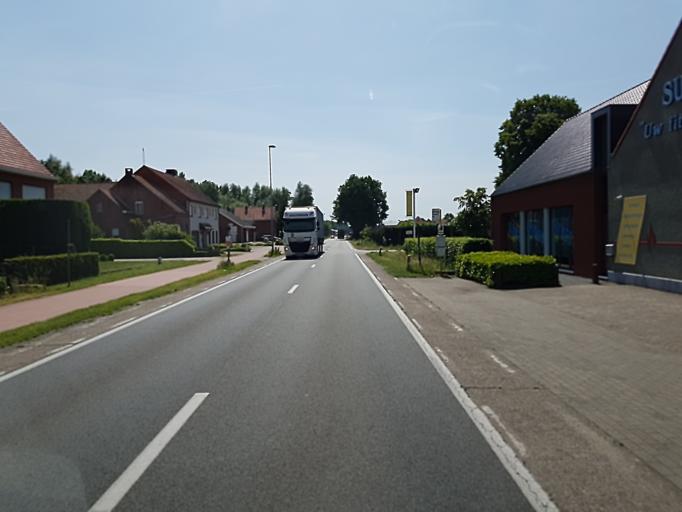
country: BE
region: Flanders
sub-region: Provincie Antwerpen
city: Retie
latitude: 51.2868
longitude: 5.0922
